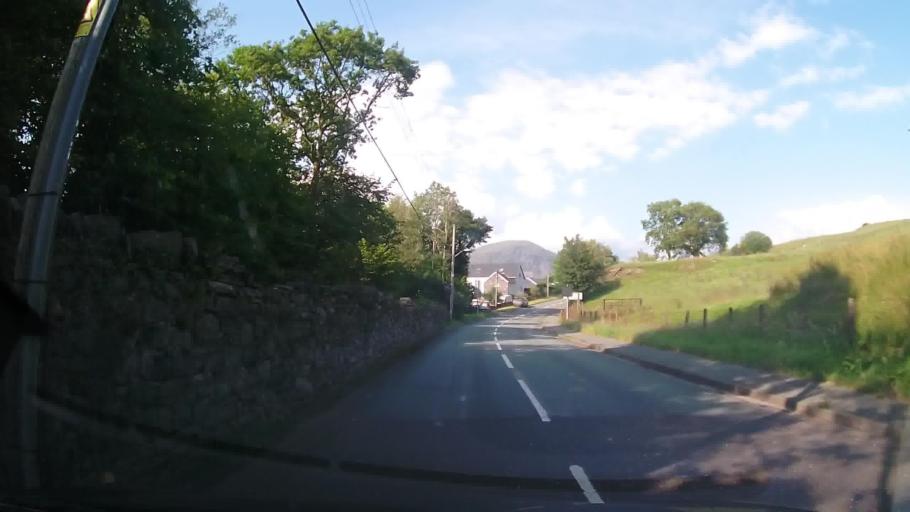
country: GB
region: Wales
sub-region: Gwynedd
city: Ffestiniog
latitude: 52.9586
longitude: -3.9302
